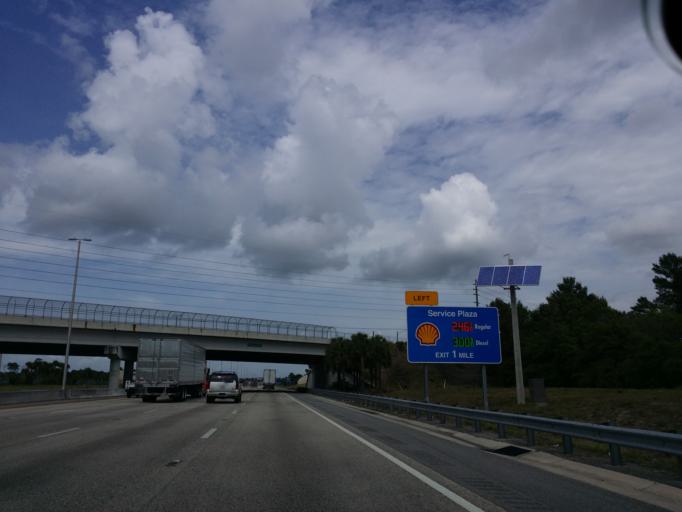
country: US
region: Florida
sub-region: Orange County
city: Orlovista
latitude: 28.5025
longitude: -81.4829
